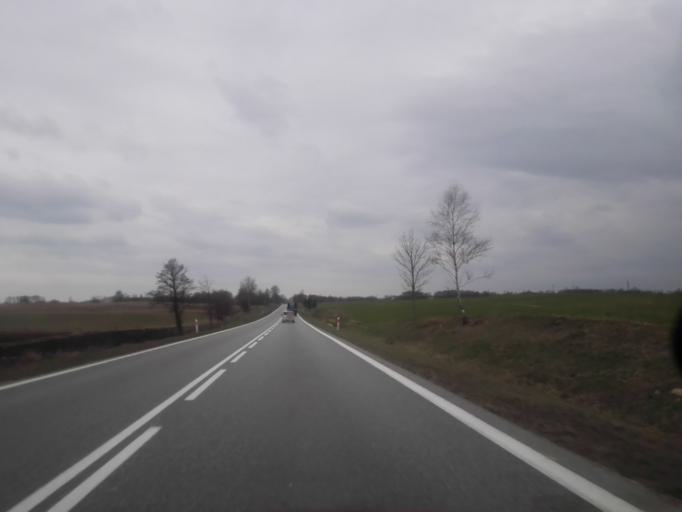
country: PL
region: Podlasie
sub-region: Powiat augustowski
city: Augustow
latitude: 53.8116
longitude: 22.9128
